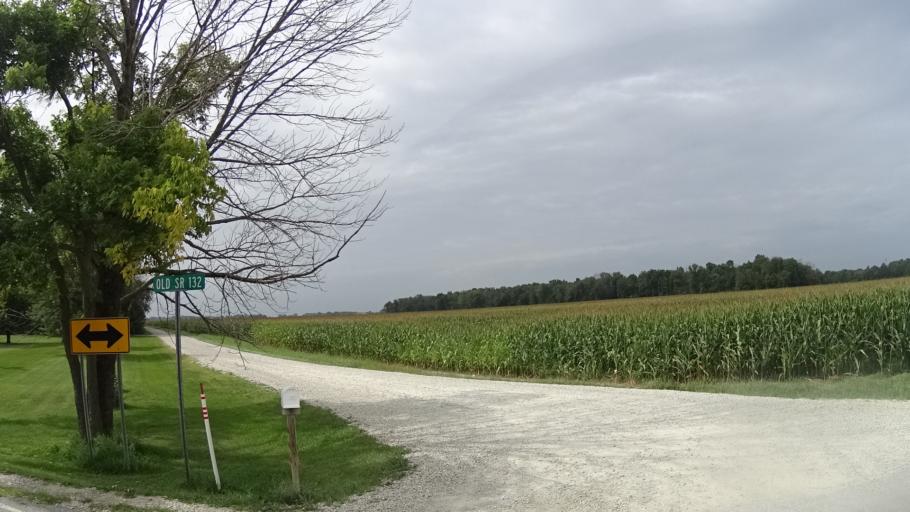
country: US
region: Indiana
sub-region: Madison County
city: Pendleton
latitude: 40.0216
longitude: -85.7725
